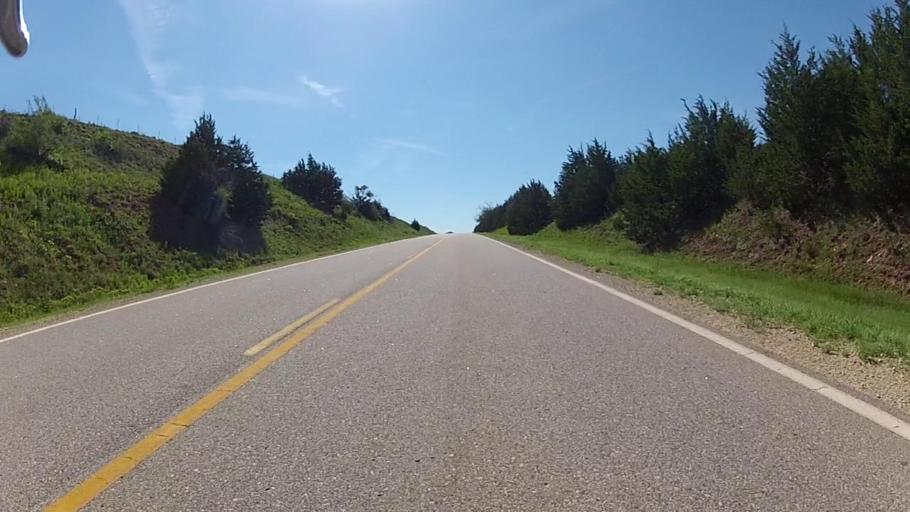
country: US
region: Kansas
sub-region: Barber County
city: Medicine Lodge
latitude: 37.2790
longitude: -98.7420
